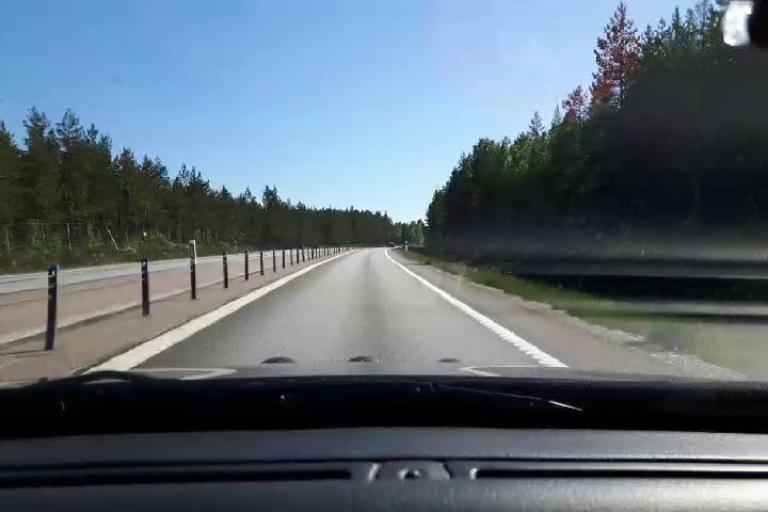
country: SE
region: Gaevleborg
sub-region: Soderhamns Kommun
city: Ljusne
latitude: 61.1167
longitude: 17.0133
